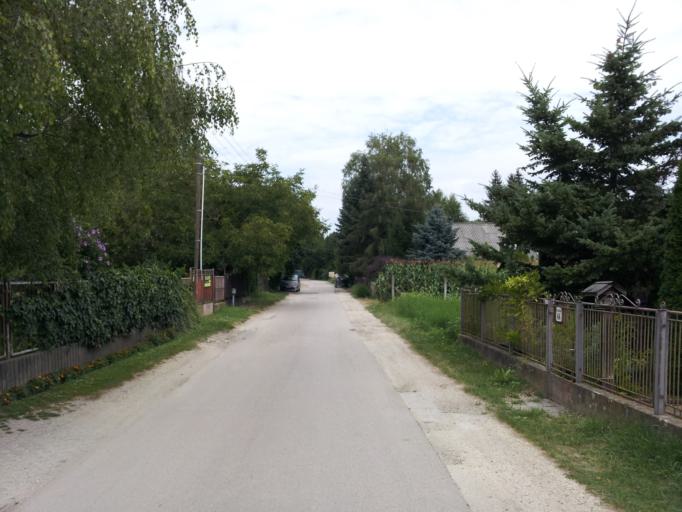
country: HU
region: Pest
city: Rackeve
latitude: 47.1691
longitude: 18.9513
